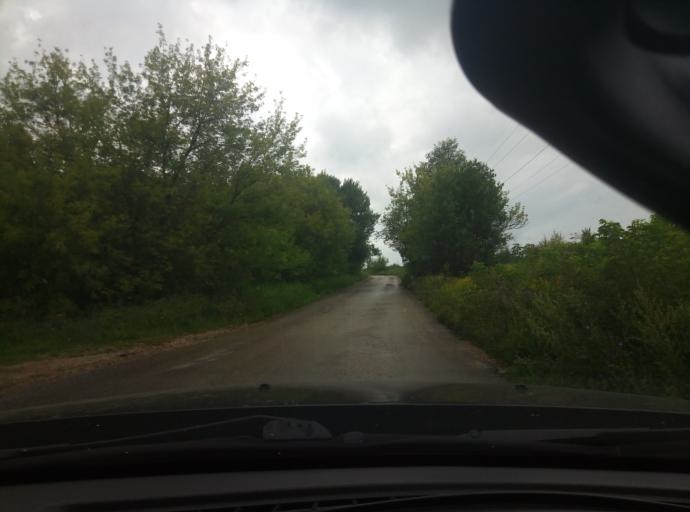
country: RU
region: Tula
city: Lomintsevskiy
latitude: 53.9528
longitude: 37.6444
